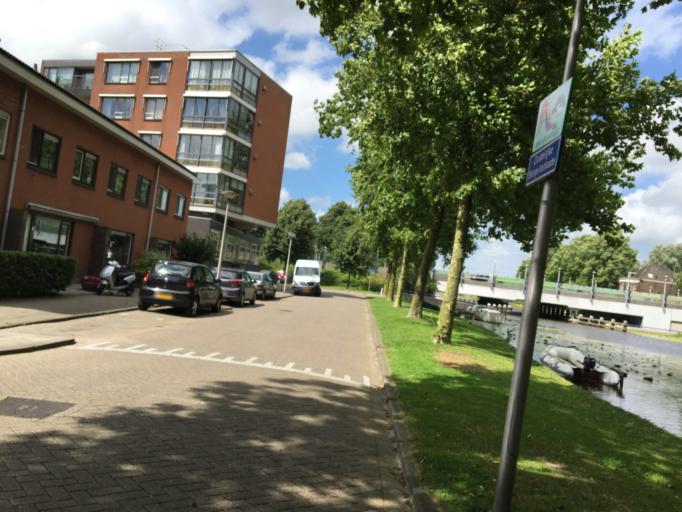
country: NL
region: South Holland
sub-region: Gemeente Gouda
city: Gouda
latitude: 52.0155
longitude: 4.7220
